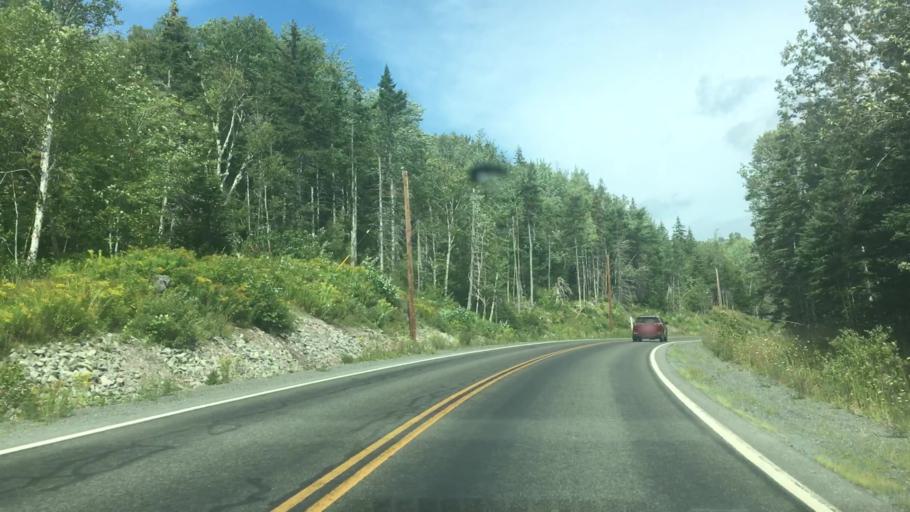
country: CA
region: Nova Scotia
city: Sydney Mines
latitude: 46.2074
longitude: -60.6228
